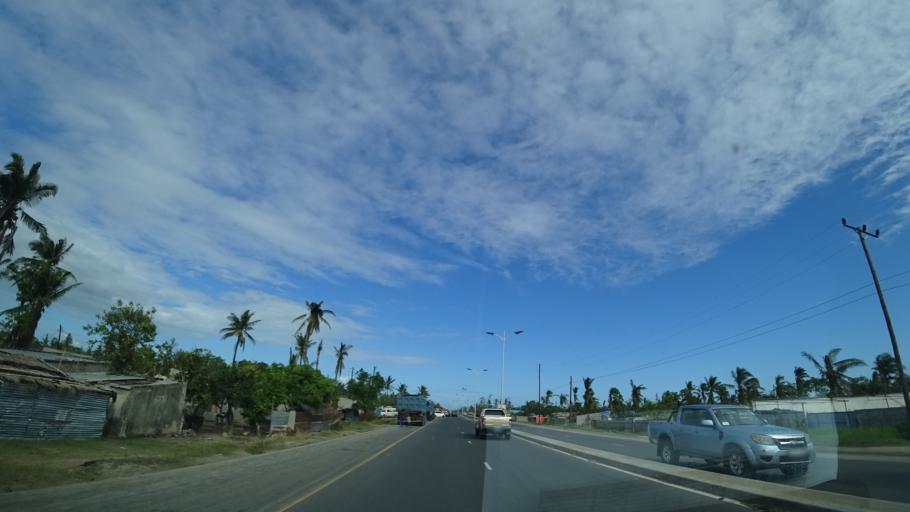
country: MZ
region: Sofala
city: Beira
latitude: -19.7573
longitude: 34.8780
